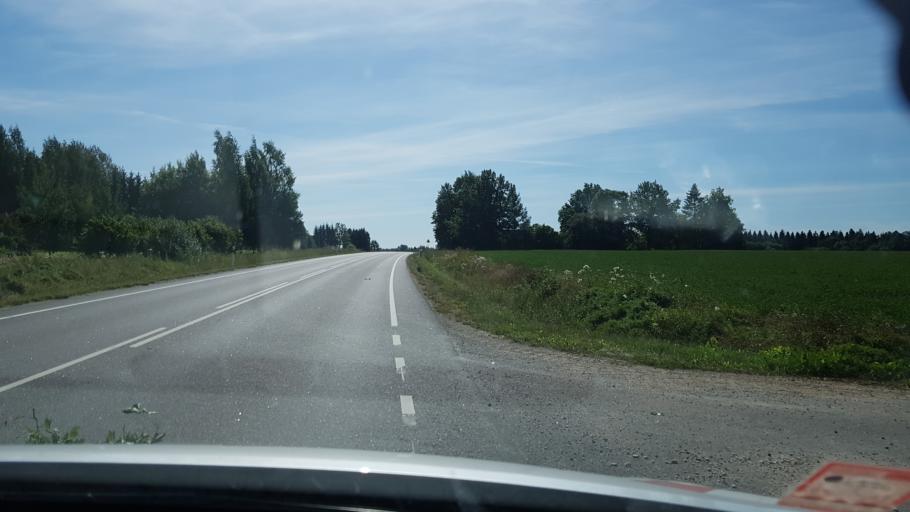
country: EE
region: Tartu
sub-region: Tartu linn
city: Tartu
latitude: 58.4110
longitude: 26.8920
